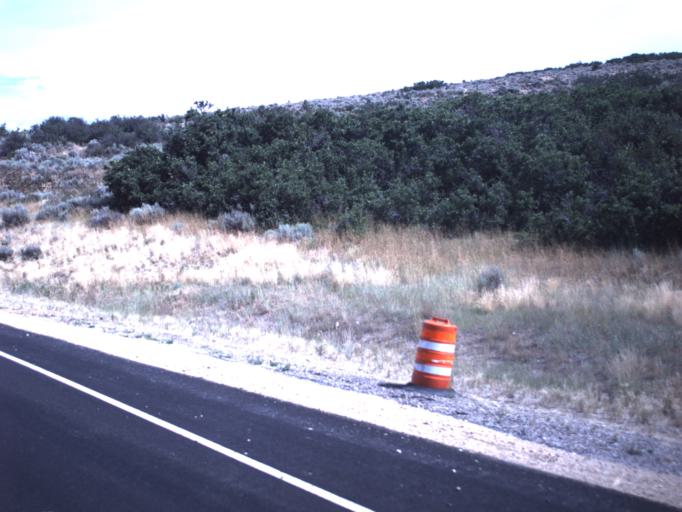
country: US
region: Utah
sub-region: Summit County
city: Park City
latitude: 40.6653
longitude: -111.4184
